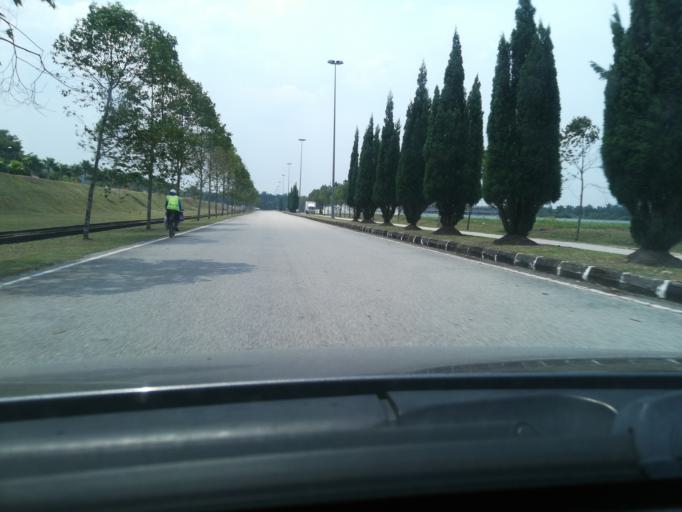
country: MY
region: Kedah
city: Kulim
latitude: 5.4269
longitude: 100.5775
